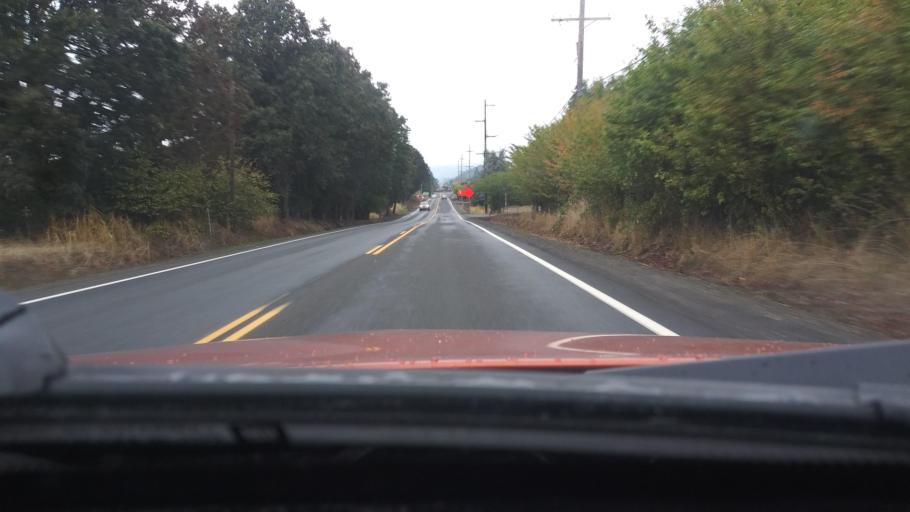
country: US
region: Oregon
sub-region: Washington County
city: Banks
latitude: 45.6042
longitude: -123.1145
